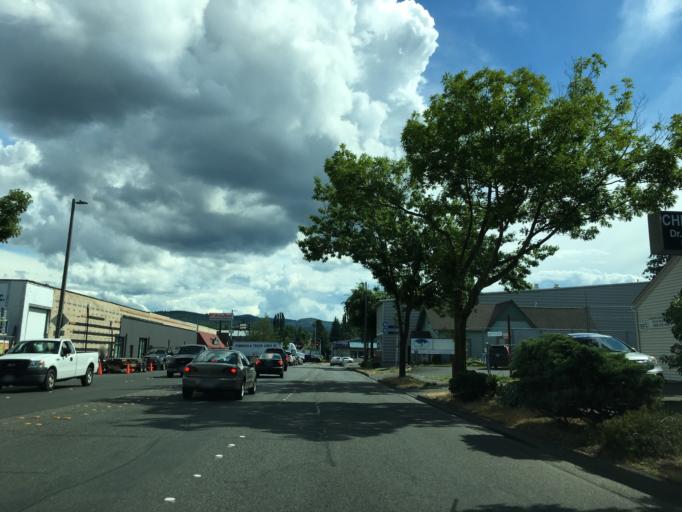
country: US
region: Washington
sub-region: Whatcom County
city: Bellingham
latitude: 48.7576
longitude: -122.4650
